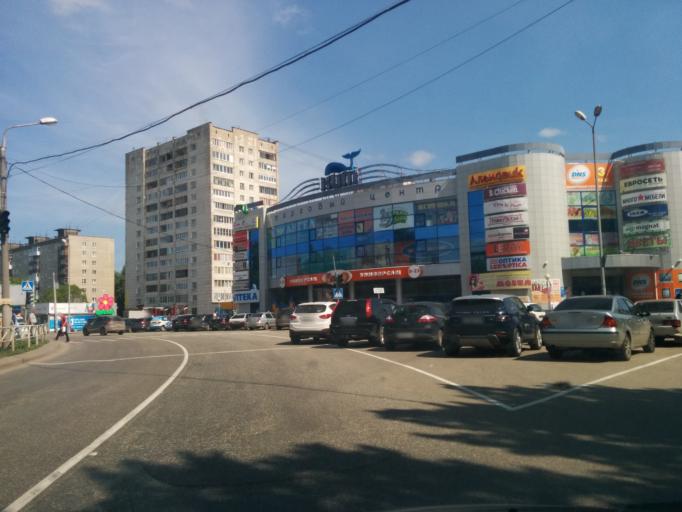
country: RU
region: Perm
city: Perm
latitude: 57.9978
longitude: 56.2928
